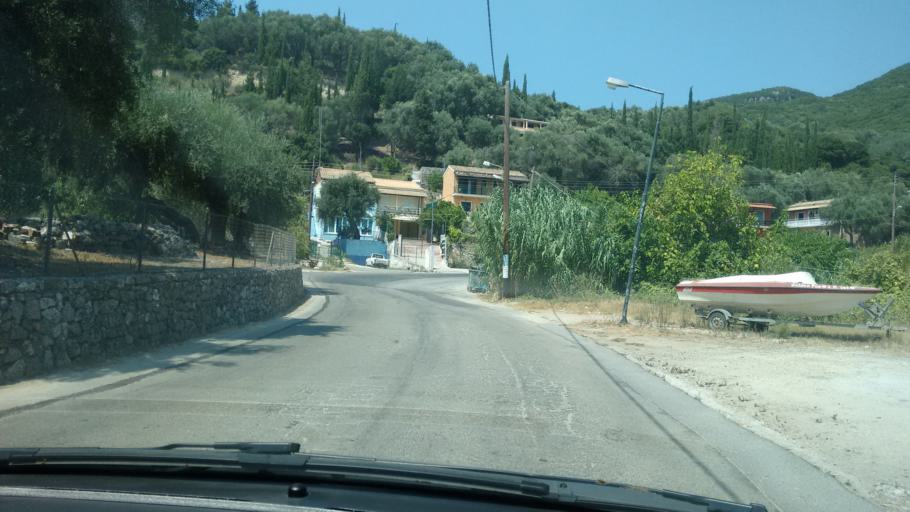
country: GR
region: Ionian Islands
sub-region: Nomos Kerkyras
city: Agios Georgis
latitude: 39.6759
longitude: 19.7252
